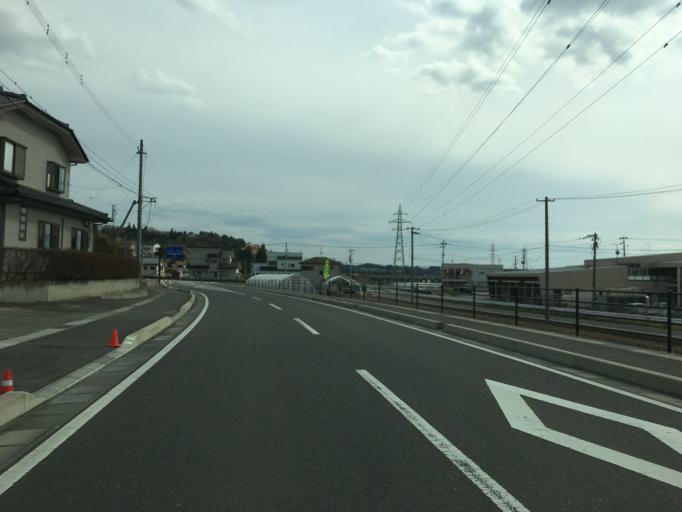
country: JP
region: Fukushima
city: Nihommatsu
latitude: 37.6118
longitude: 140.4680
